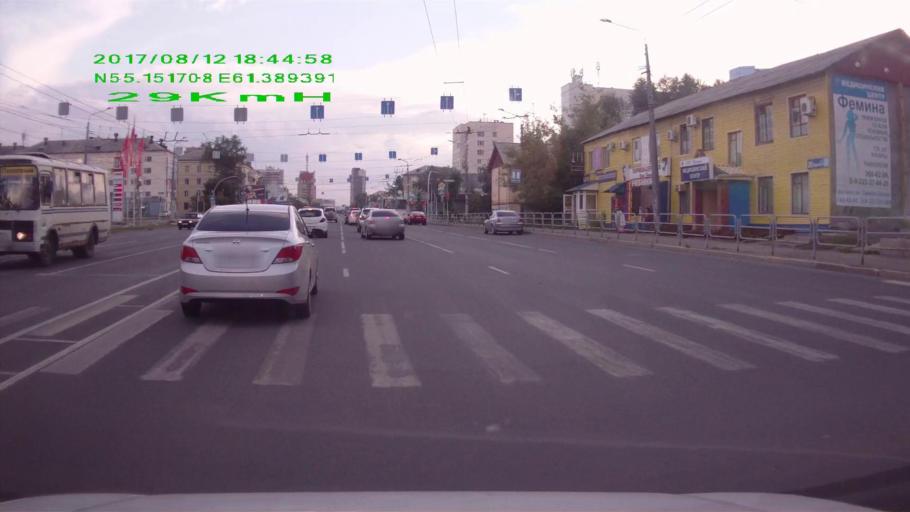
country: RU
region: Chelyabinsk
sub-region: Gorod Chelyabinsk
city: Chelyabinsk
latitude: 55.1493
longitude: 61.3851
